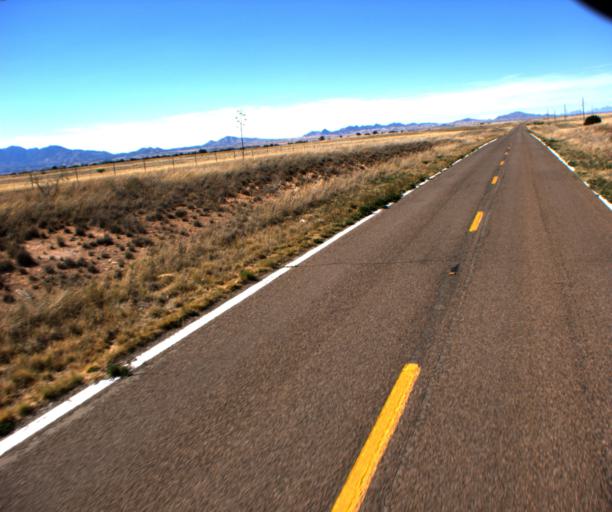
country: US
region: Arizona
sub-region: Cochise County
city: Huachuca City
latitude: 31.6330
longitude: -110.5962
